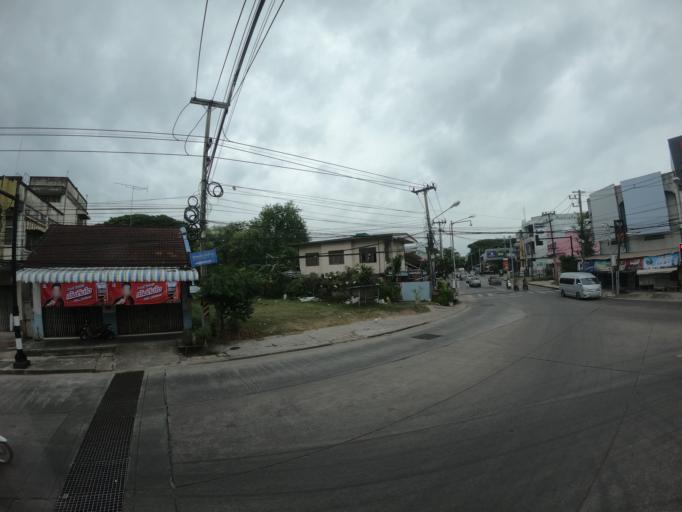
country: TH
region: Roi Et
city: Roi Et
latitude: 16.0515
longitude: 103.6418
